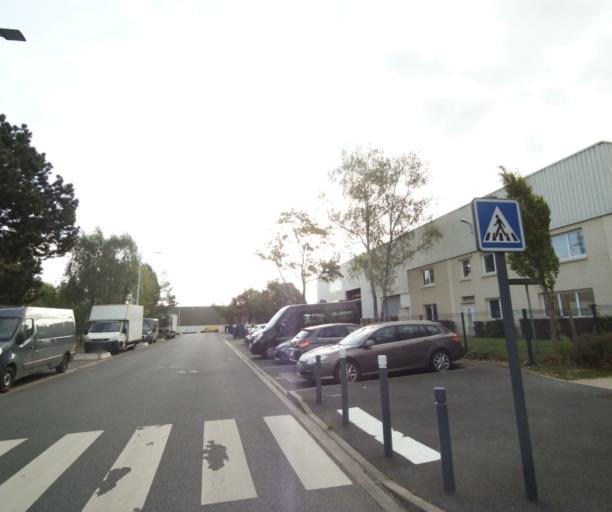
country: FR
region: Ile-de-France
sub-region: Departement de Seine-et-Marne
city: Torcy
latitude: 48.8449
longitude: 2.6586
